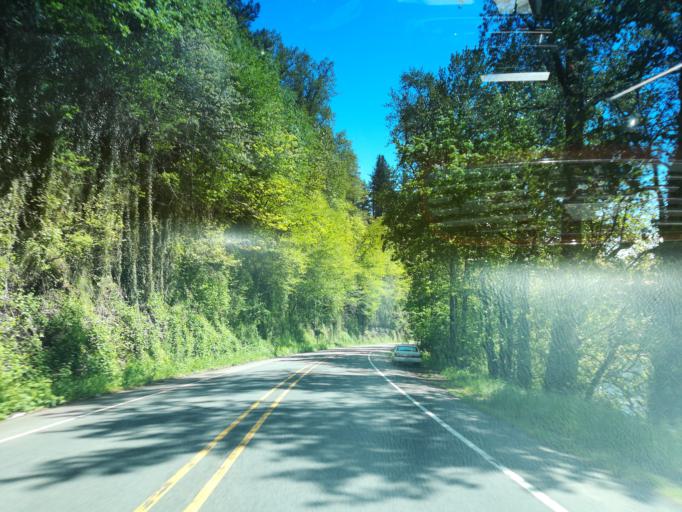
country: US
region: Oregon
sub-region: Multnomah County
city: Troutdale
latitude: 45.5239
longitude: -122.3698
